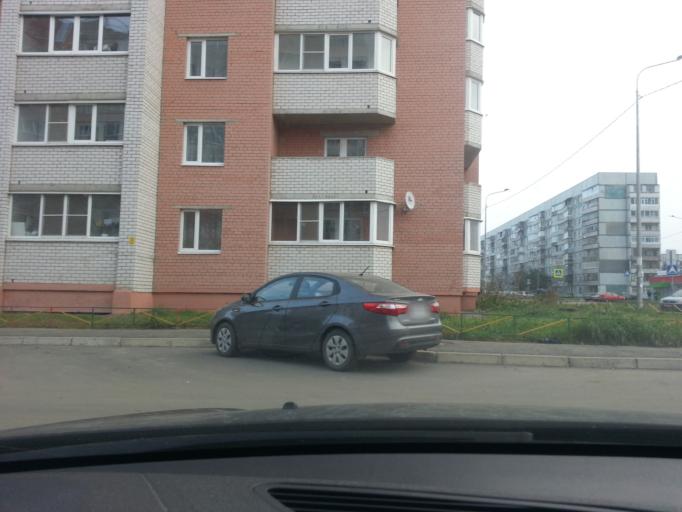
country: RU
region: Vologda
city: Vologda
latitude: 59.2223
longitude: 39.9332
